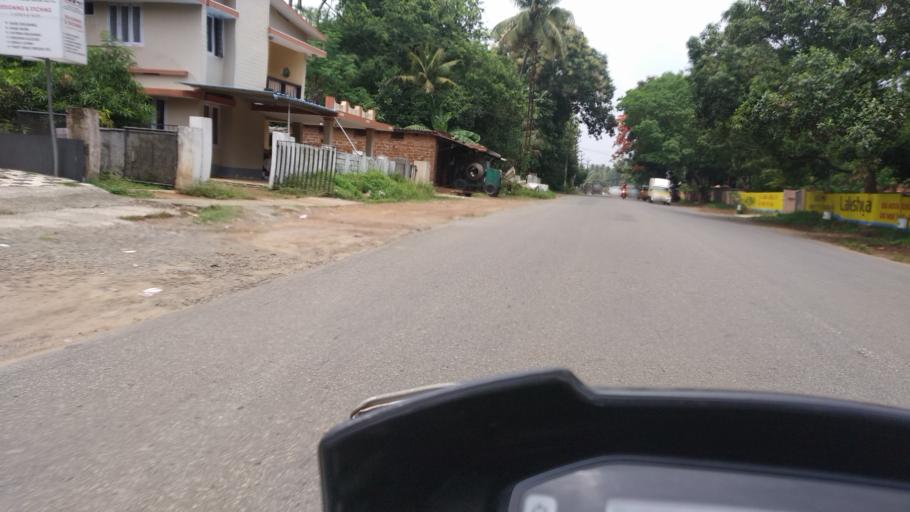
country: IN
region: Kerala
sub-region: Ernakulam
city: Perumpavur
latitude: 10.1128
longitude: 76.5109
